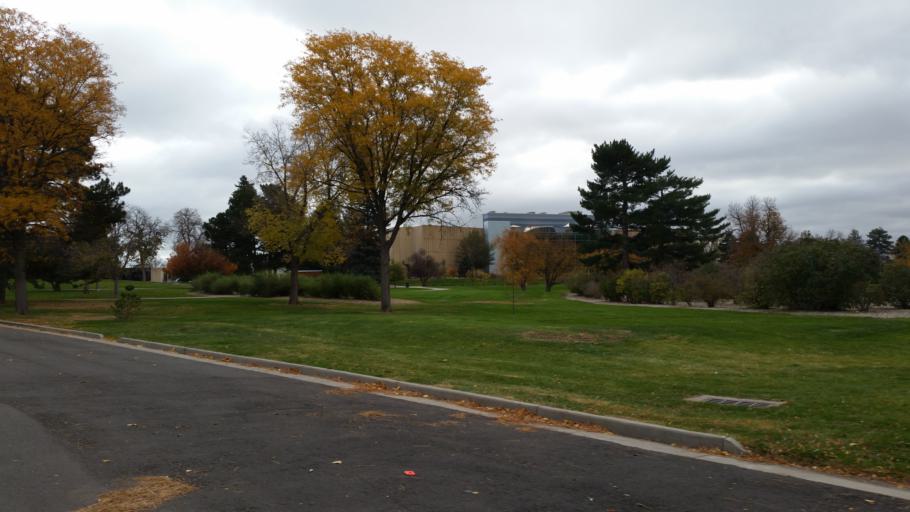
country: US
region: Colorado
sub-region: Denver County
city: Denver
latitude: 39.7482
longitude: -104.9466
